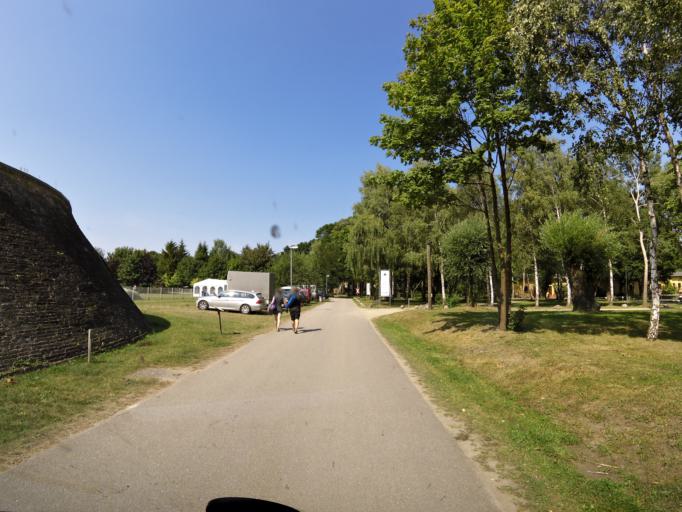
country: DE
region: Brandenburg
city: Zehdenick
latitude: 53.0318
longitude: 13.3102
